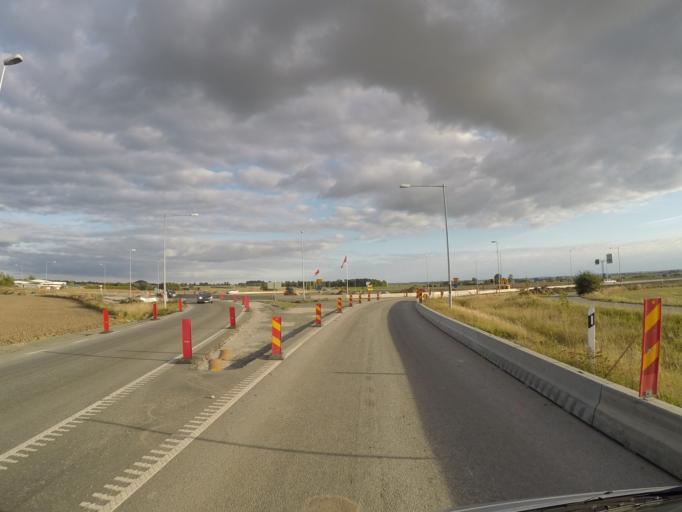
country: SE
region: Skane
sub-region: Lunds Kommun
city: Genarp
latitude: 55.6624
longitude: 13.3330
